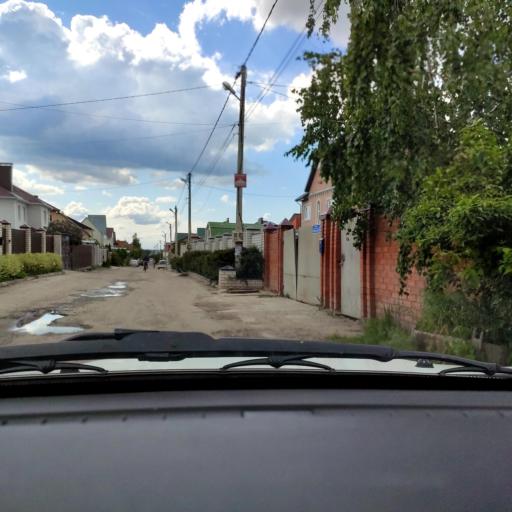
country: RU
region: Voronezj
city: Podgornoye
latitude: 51.7459
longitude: 39.1558
